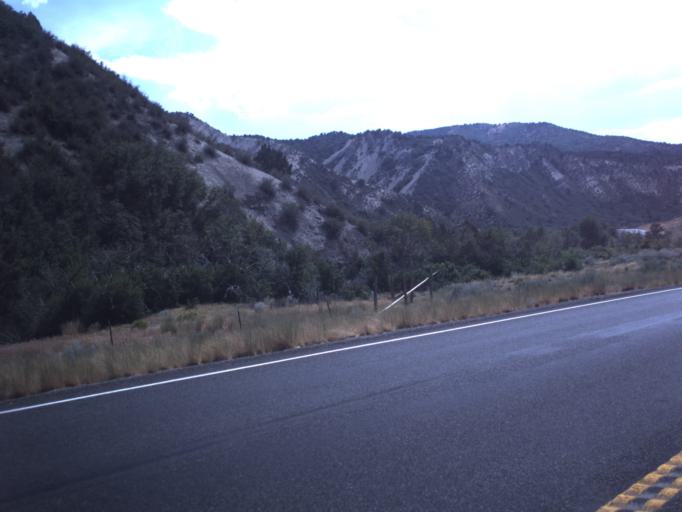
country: US
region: Utah
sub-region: Juab County
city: Nephi
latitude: 39.7161
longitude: -111.7673
